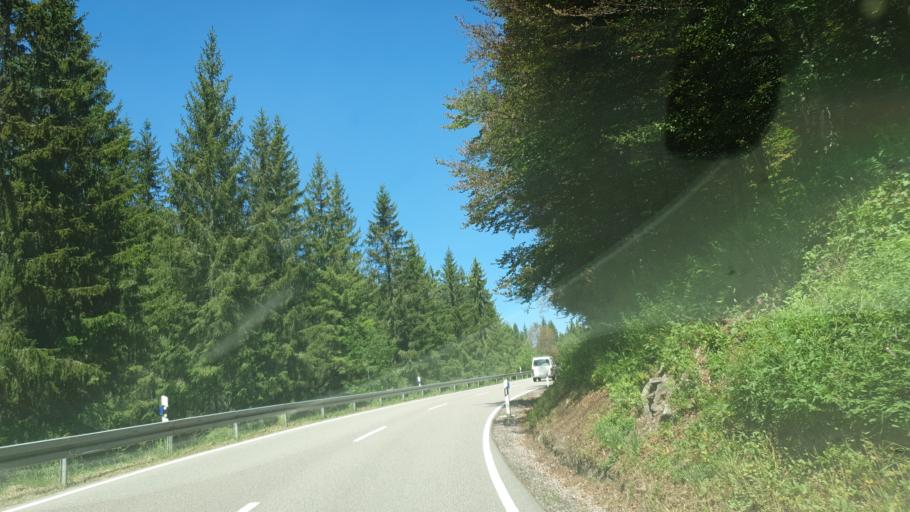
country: DE
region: Baden-Wuerttemberg
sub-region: Freiburg Region
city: Wieden
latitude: 47.8725
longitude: 7.9128
